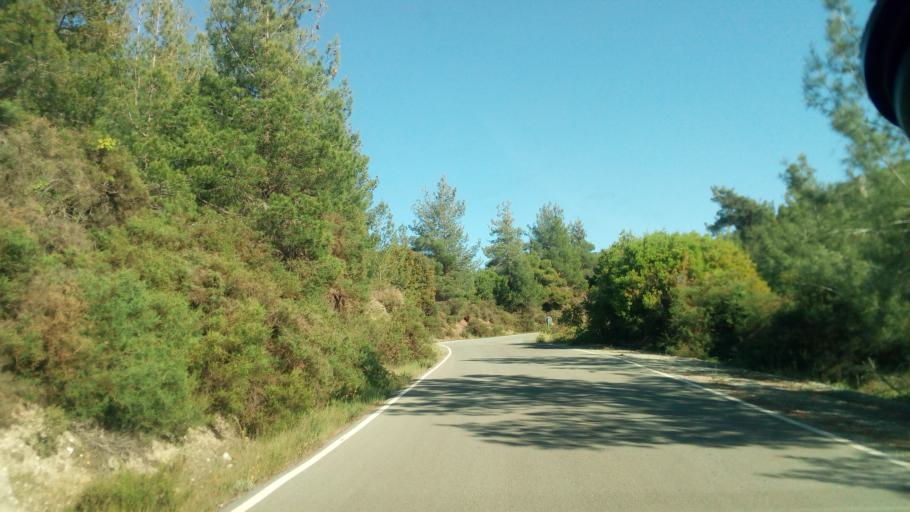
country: CY
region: Limassol
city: Pachna
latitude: 34.8853
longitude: 32.7512
